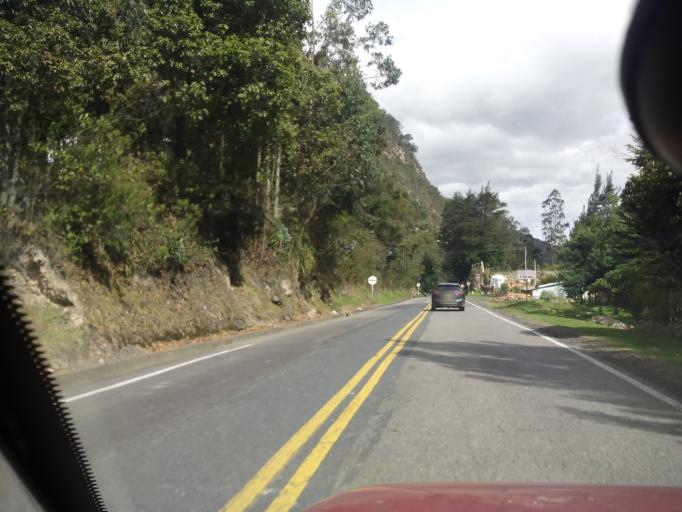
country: CO
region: Boyaca
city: Arcabuco
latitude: 5.7388
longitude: -73.4146
